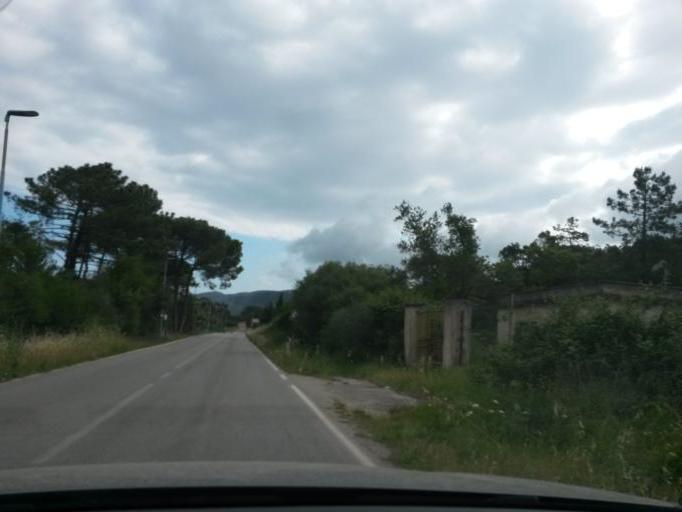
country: IT
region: Tuscany
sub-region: Provincia di Livorno
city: Portoferraio
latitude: 42.7920
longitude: 10.3511
